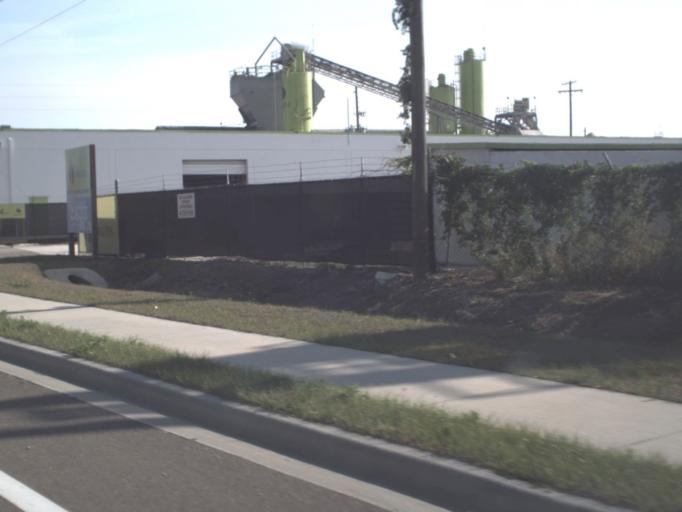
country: US
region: Florida
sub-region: Orange County
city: Fairview Shores
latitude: 28.6038
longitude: -81.4179
